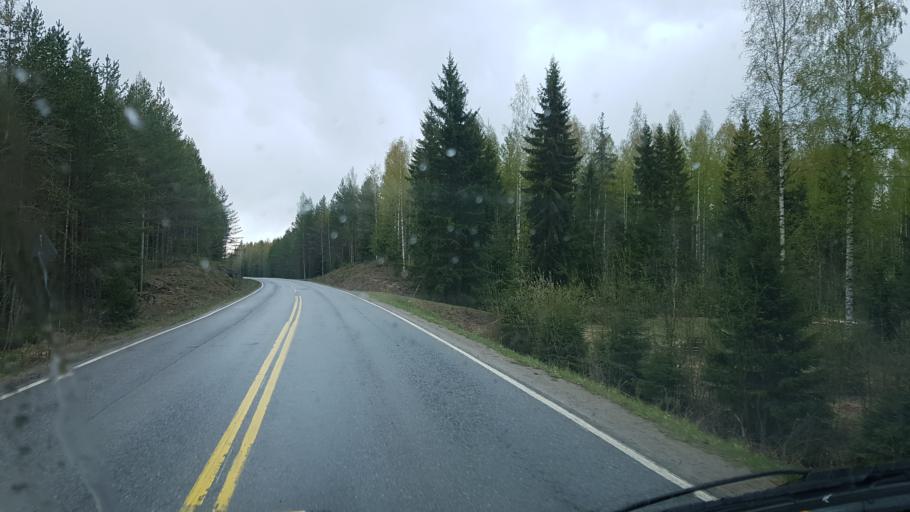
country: FI
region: Pirkanmaa
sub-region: Tampere
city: Pirkkala
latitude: 61.3967
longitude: 23.6271
